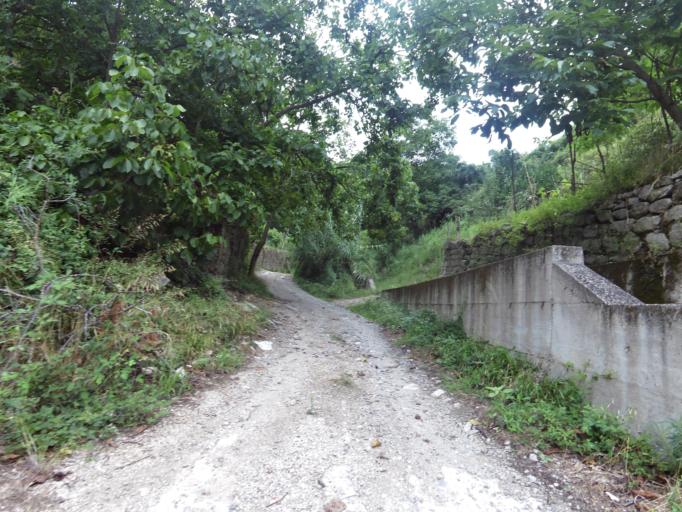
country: IT
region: Calabria
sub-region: Provincia di Reggio Calabria
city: Bivongi
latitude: 38.4894
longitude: 16.4293
